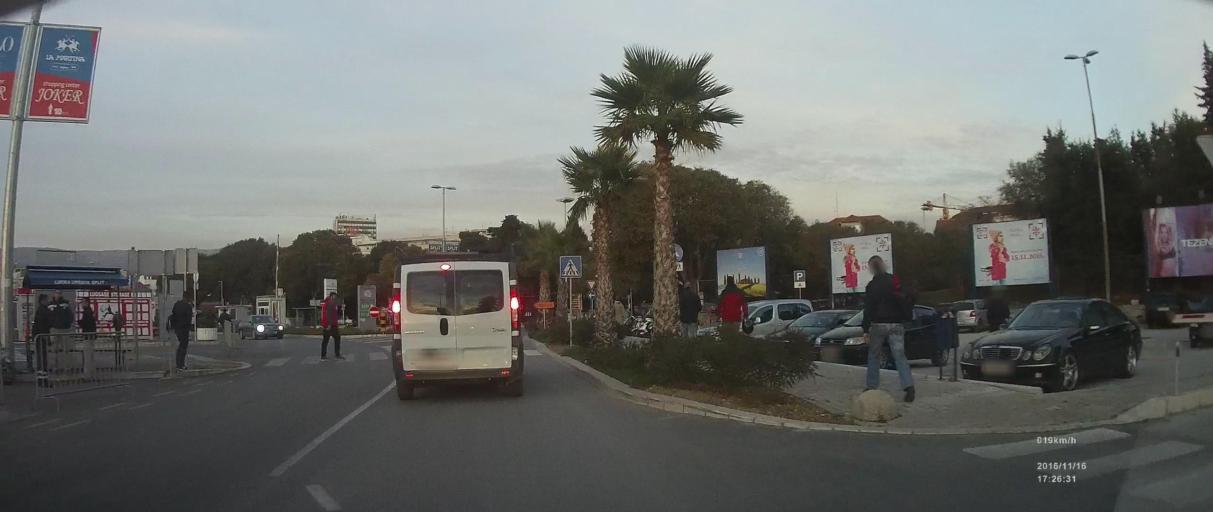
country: HR
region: Splitsko-Dalmatinska
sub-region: Grad Split
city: Split
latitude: 43.5024
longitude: 16.4427
